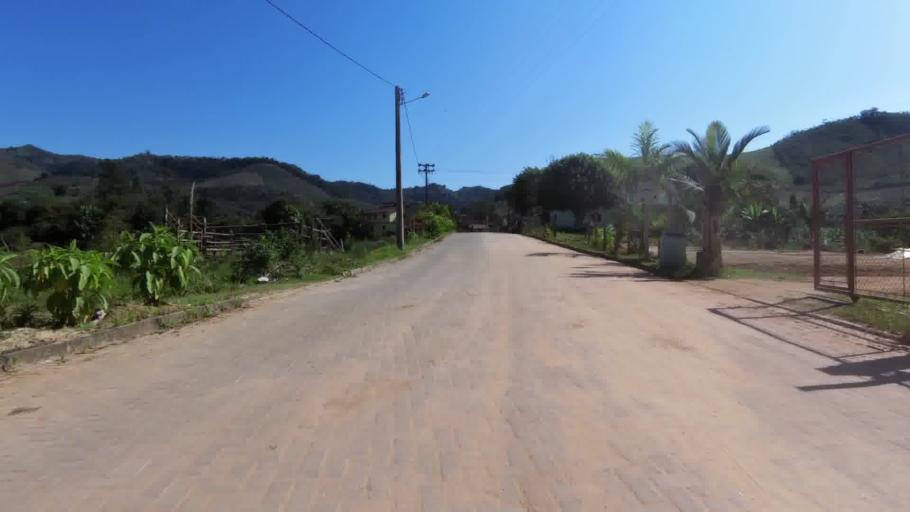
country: BR
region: Espirito Santo
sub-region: Alfredo Chaves
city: Alfredo Chaves
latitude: -20.5343
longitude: -40.8367
